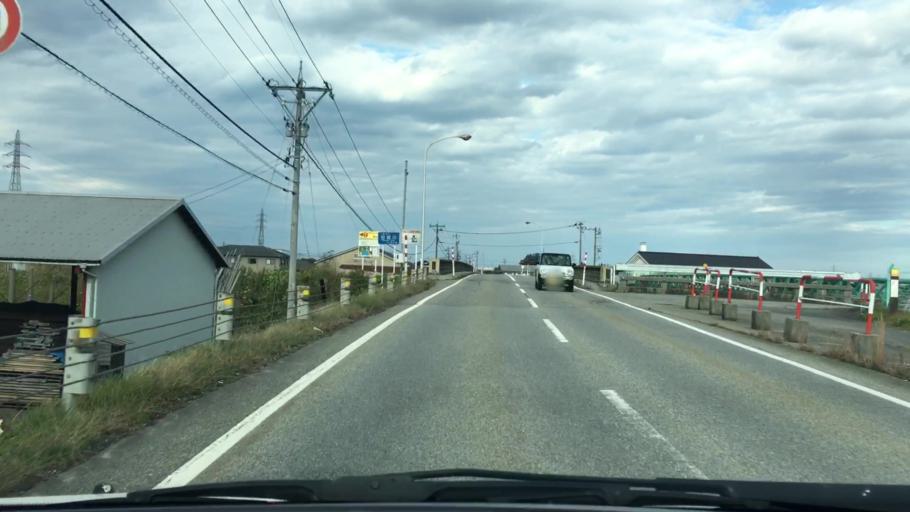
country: JP
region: Toyama
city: Kamiichi
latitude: 36.7055
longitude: 137.3166
